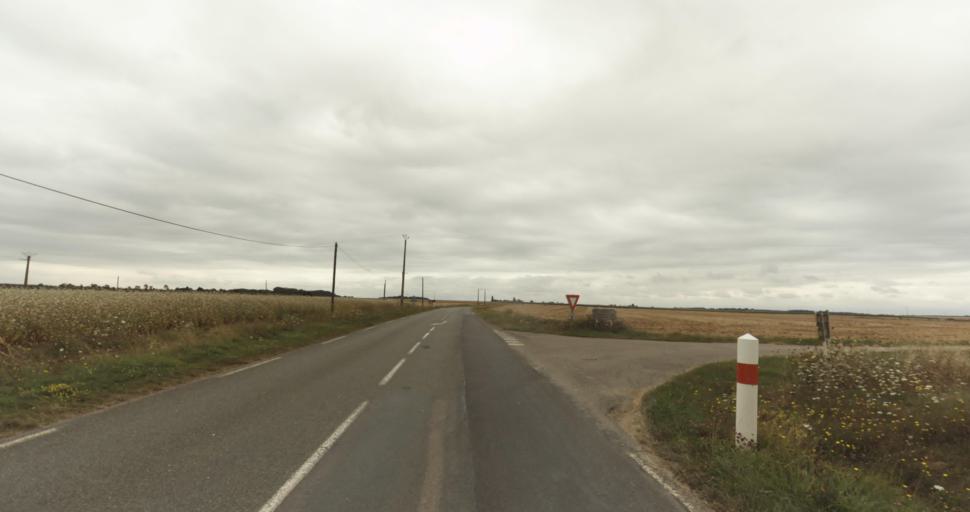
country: FR
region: Haute-Normandie
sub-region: Departement de l'Eure
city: Gravigny
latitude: 49.0551
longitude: 1.2446
